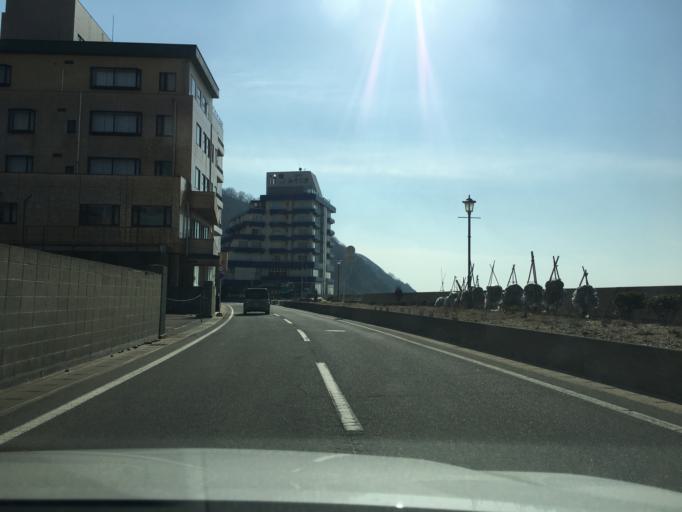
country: JP
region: Yamagata
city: Tsuruoka
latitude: 38.7793
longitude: 139.7503
